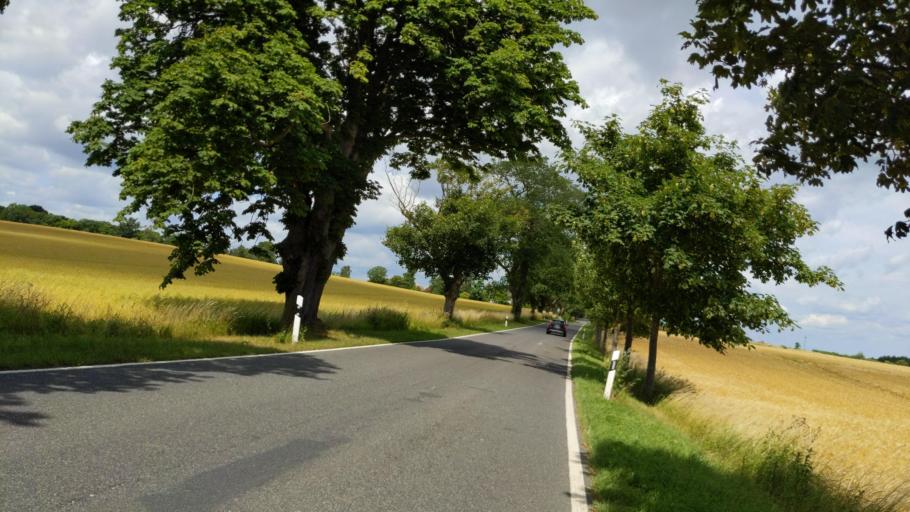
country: DE
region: Mecklenburg-Vorpommern
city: Dassow
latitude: 53.9283
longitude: 10.9728
